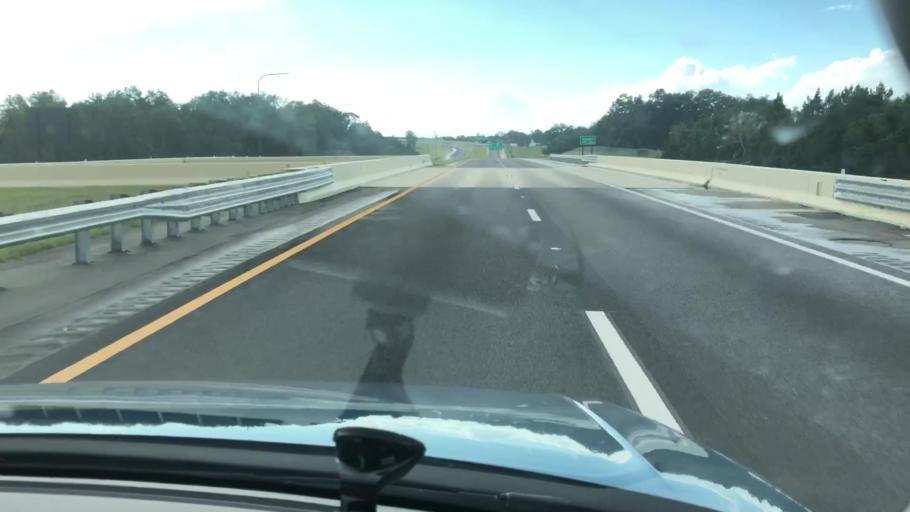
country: US
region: Florida
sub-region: Lake County
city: Mount Plymouth
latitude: 28.7759
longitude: -81.5445
